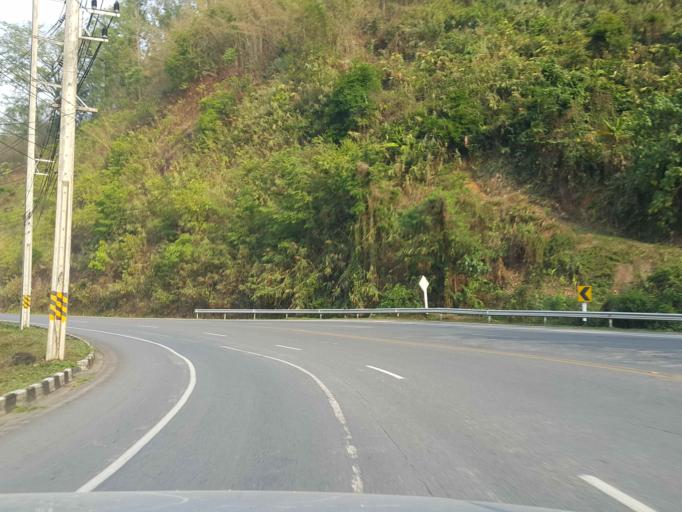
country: TH
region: Chiang Mai
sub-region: Amphoe Chiang Dao
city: Chiang Dao
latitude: 19.2529
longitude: 98.9681
